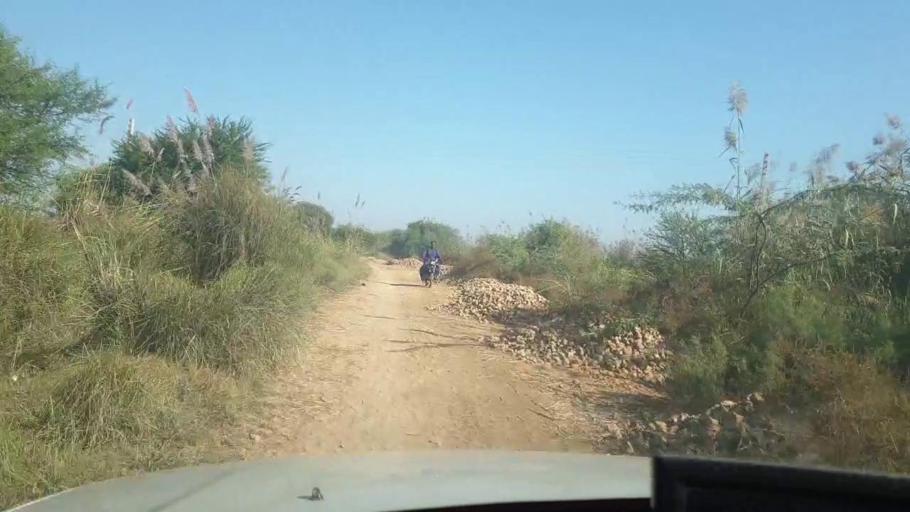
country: PK
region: Sindh
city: Mirpur Sakro
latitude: 24.5025
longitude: 67.6231
